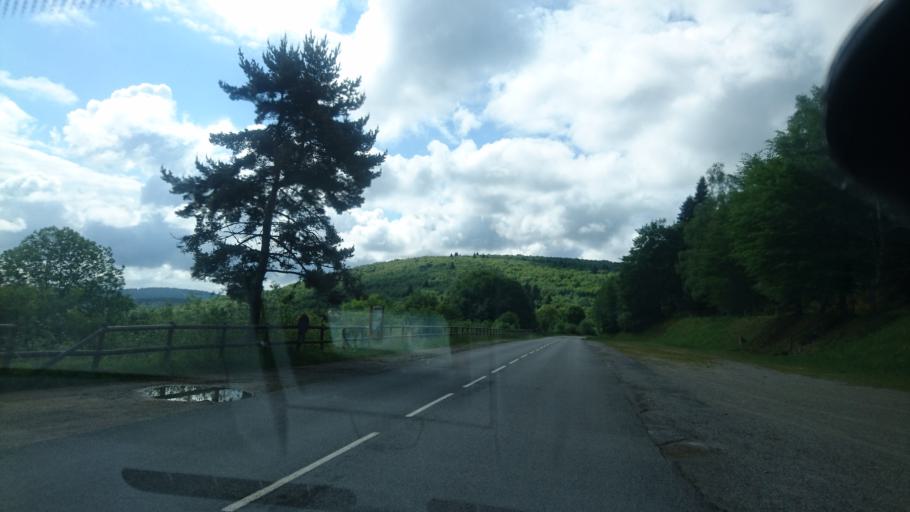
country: FR
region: Limousin
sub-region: Departement de la Haute-Vienne
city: Peyrat-le-Chateau
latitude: 45.7991
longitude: 1.8406
